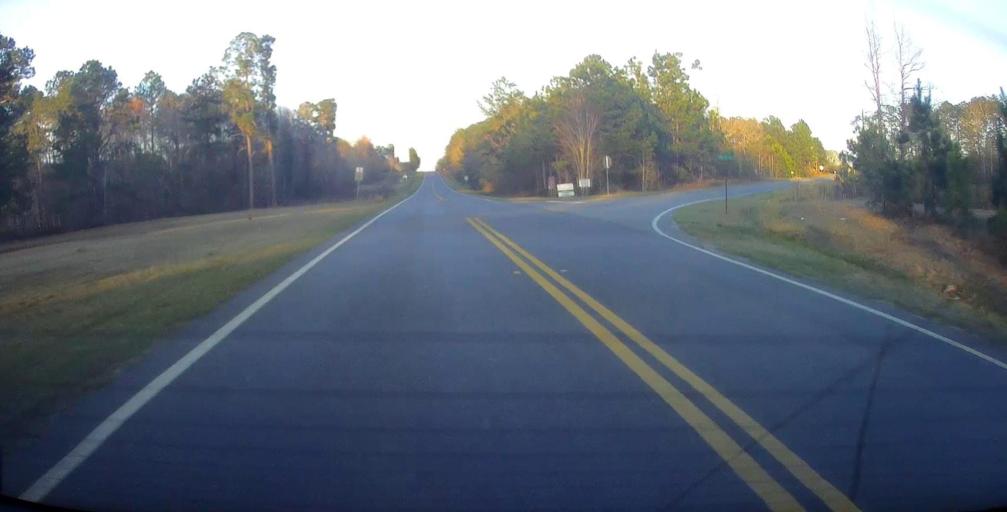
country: US
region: Georgia
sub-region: Dodge County
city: Chester
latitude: 32.3474
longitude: -83.0353
